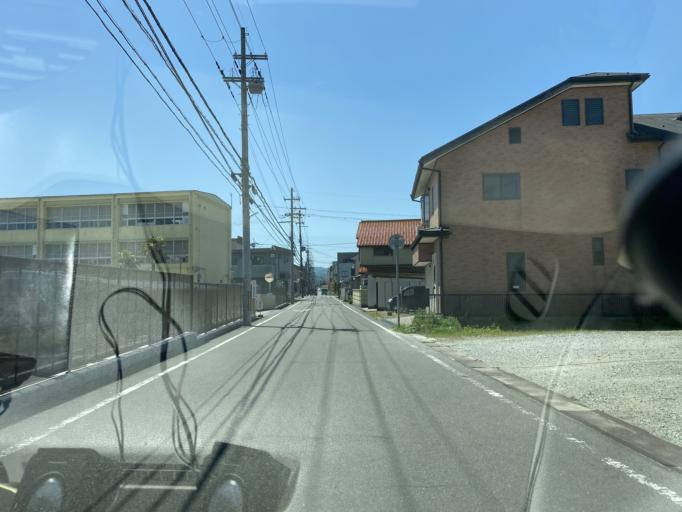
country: JP
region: Hyogo
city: Toyooka
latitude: 35.5378
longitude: 134.8197
